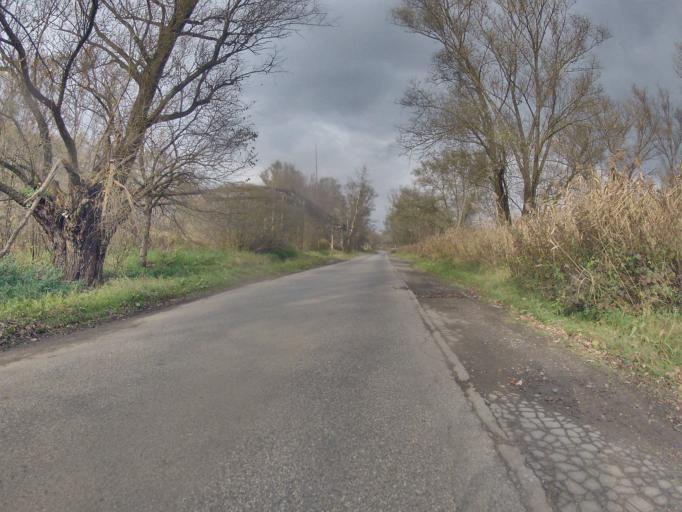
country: PL
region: Lesser Poland Voivodeship
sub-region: Powiat wielicki
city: Wegrzce Wielkie
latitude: 50.0599
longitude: 20.1023
